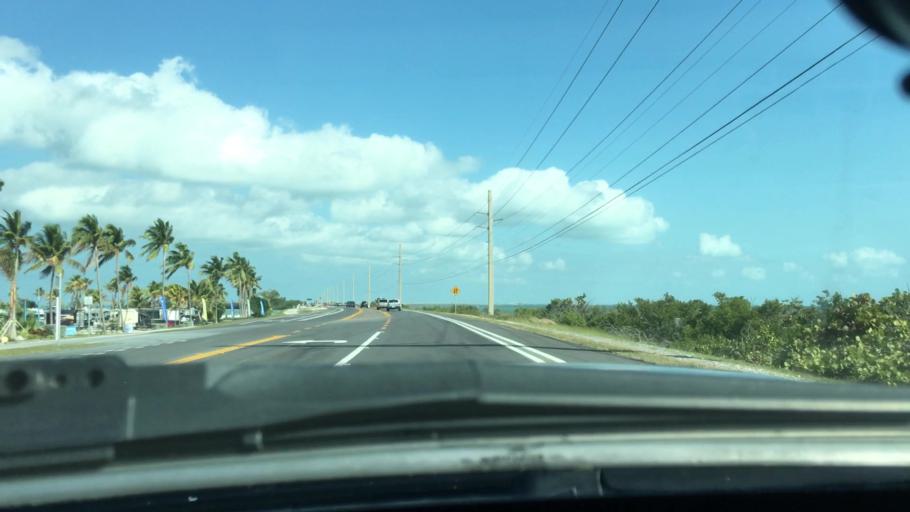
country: US
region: Florida
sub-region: Monroe County
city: Big Pine Key
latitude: 24.6716
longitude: -81.2469
